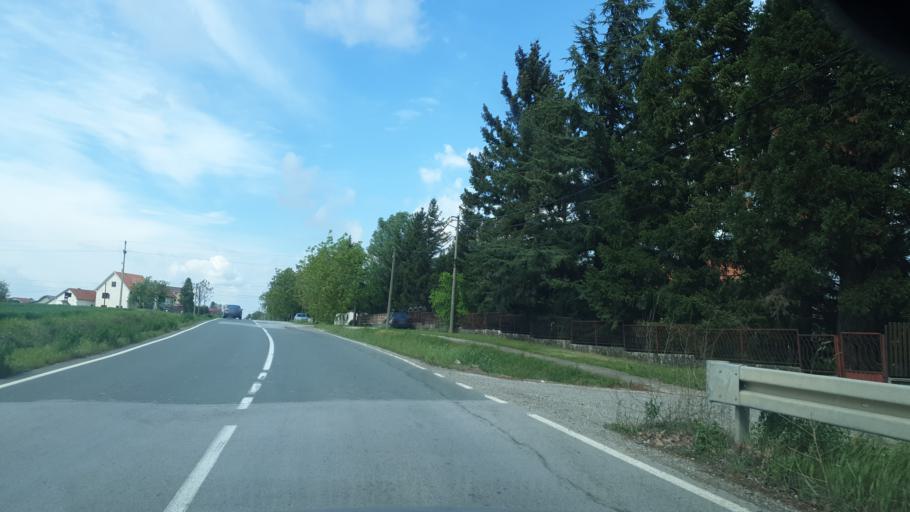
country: RS
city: Stubline
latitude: 44.5547
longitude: 20.1469
